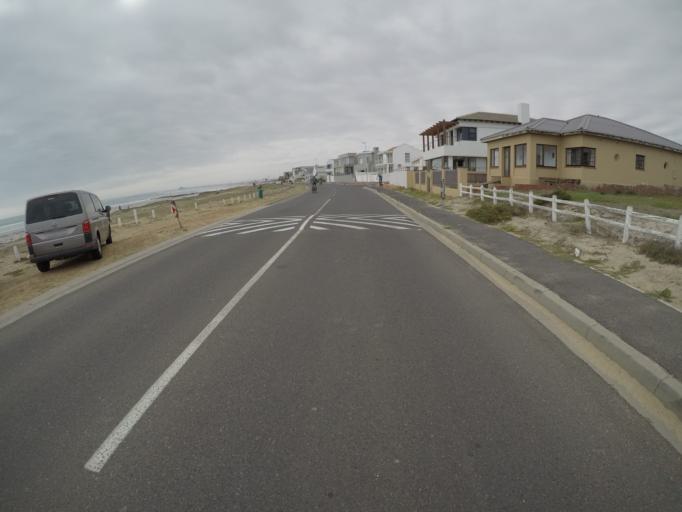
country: ZA
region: Western Cape
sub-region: City of Cape Town
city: Sunset Beach
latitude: -33.7242
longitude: 18.4433
